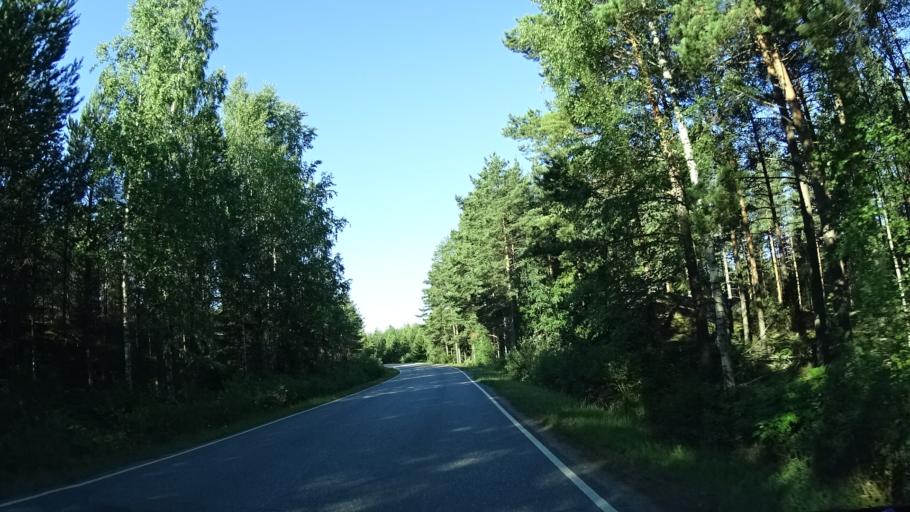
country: FI
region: Varsinais-Suomi
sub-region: Turku
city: Velkua
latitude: 60.4771
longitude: 21.7200
